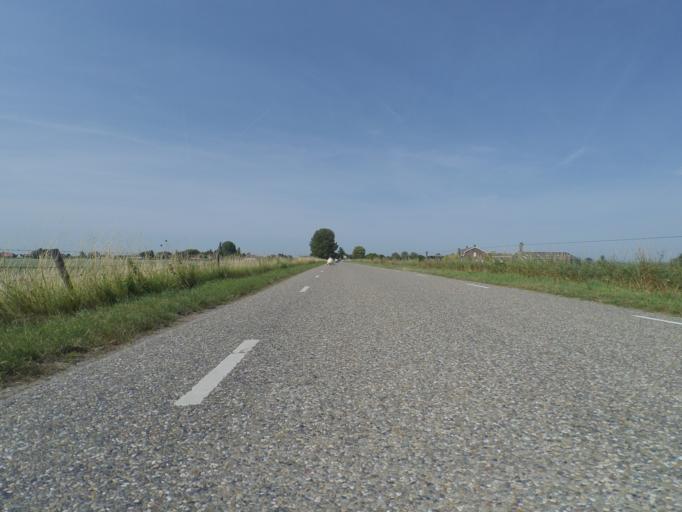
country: NL
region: North Brabant
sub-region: Gemeente Steenbergen
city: Nieuw-Vossemeer
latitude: 51.5893
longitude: 4.2514
